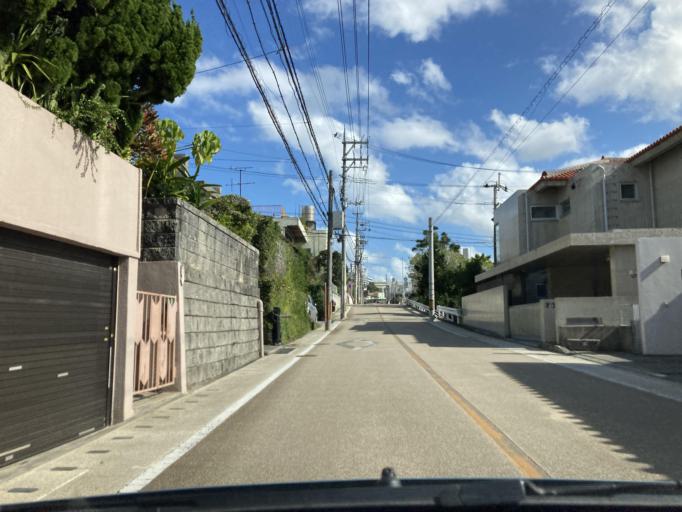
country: JP
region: Okinawa
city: Naha-shi
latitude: 26.2179
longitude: 127.7108
